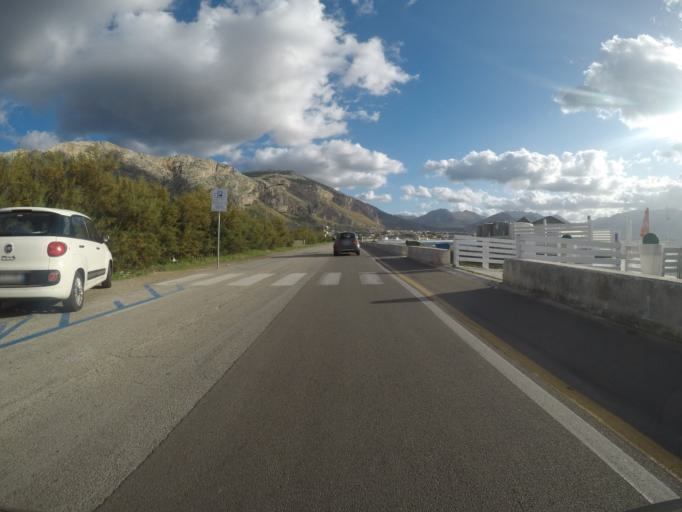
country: IT
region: Sicily
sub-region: Palermo
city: Isola delle Femmine
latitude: 38.1959
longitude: 13.2437
